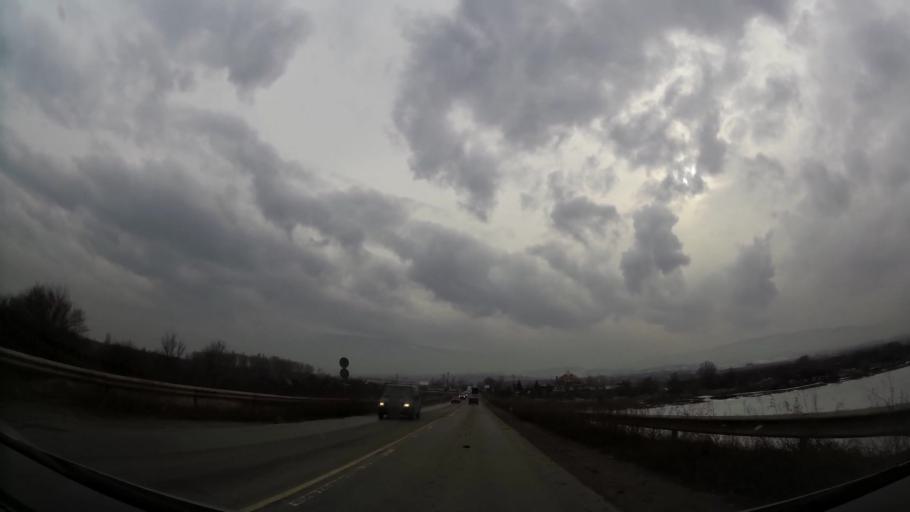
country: BG
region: Sofiya
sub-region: Obshtina Bozhurishte
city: Bozhurishte
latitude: 42.7085
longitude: 23.2305
